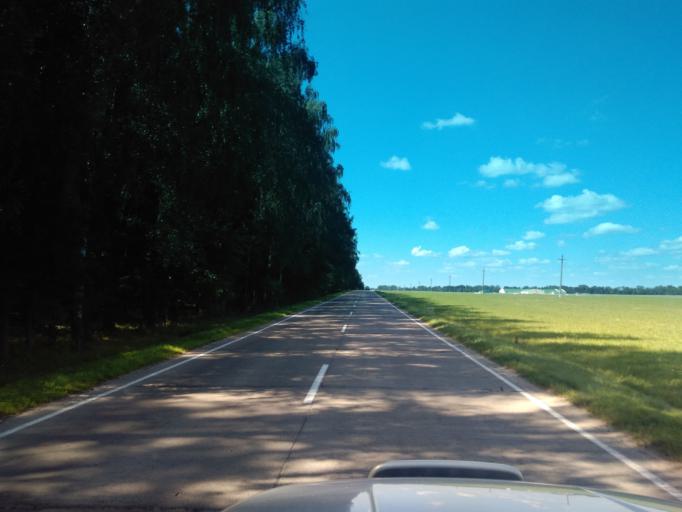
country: BY
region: Minsk
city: Stan'kava
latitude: 53.6235
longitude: 27.2892
